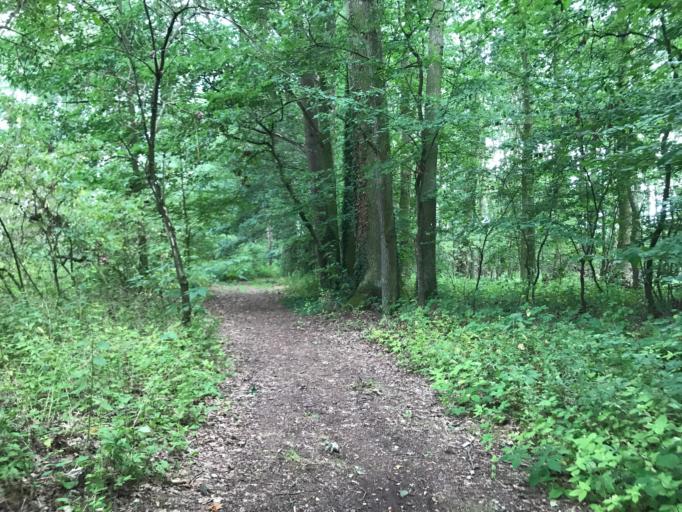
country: CZ
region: Jihocesky
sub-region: Okres Jindrichuv Hradec
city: Lomnice nad Luznici
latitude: 49.0963
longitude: 14.7163
